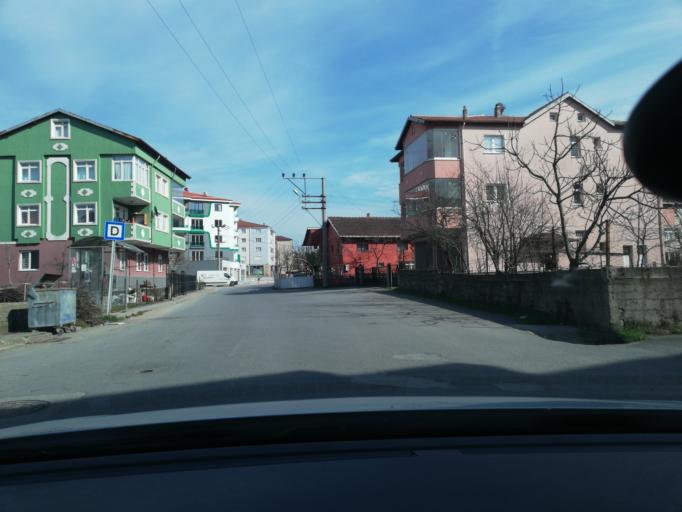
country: TR
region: Zonguldak
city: Eregli
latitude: 41.2671
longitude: 31.4521
